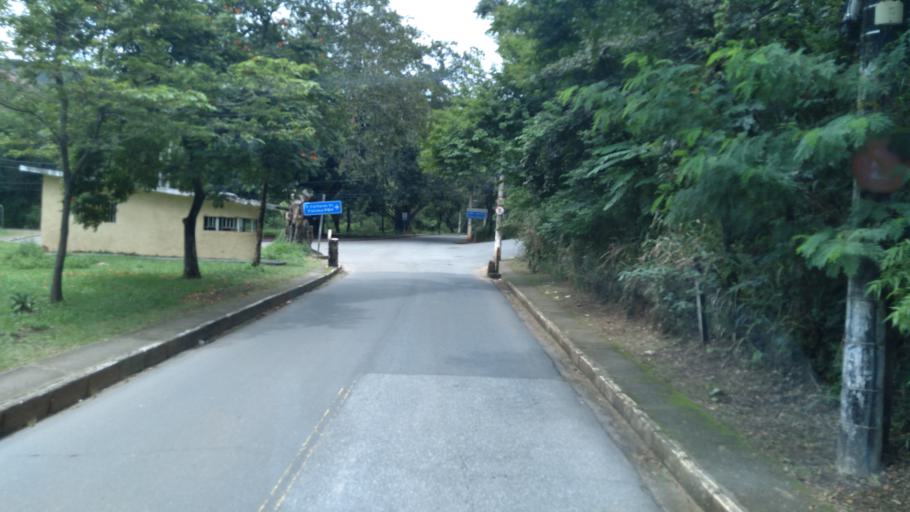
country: BR
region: Minas Gerais
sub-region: Belo Horizonte
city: Belo Horizonte
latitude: -19.9236
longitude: -43.8980
